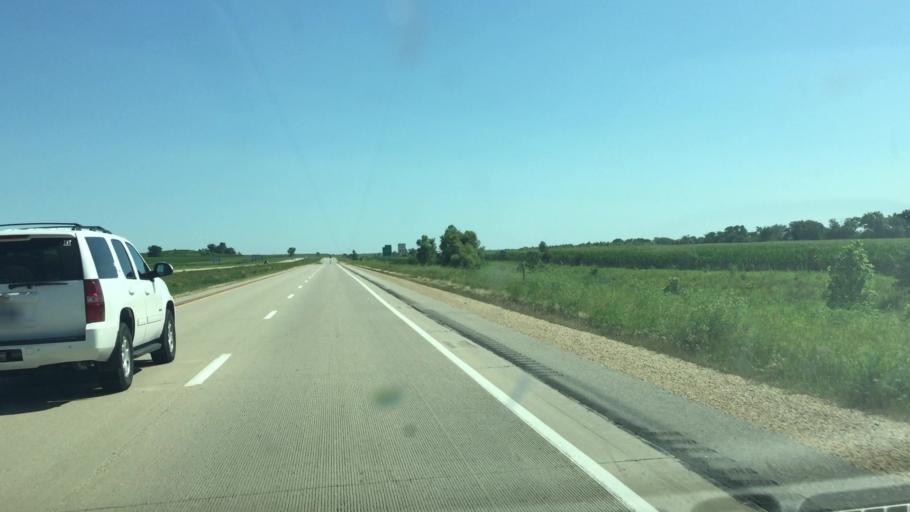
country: US
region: Iowa
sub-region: Jones County
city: Monticello
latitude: 42.2217
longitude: -91.1727
